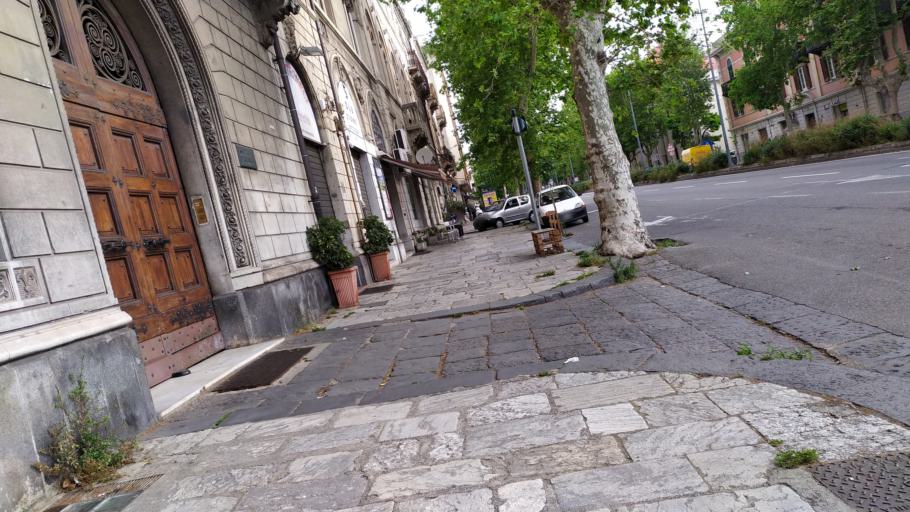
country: IT
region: Sicily
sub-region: Messina
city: Messina
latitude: 38.1999
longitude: 15.5573
